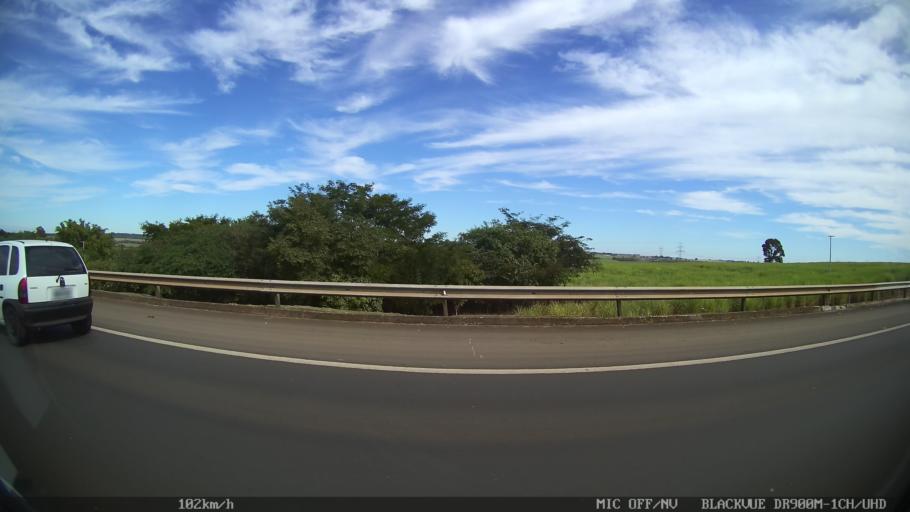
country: BR
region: Sao Paulo
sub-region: Matao
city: Matao
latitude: -21.5702
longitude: -48.4624
